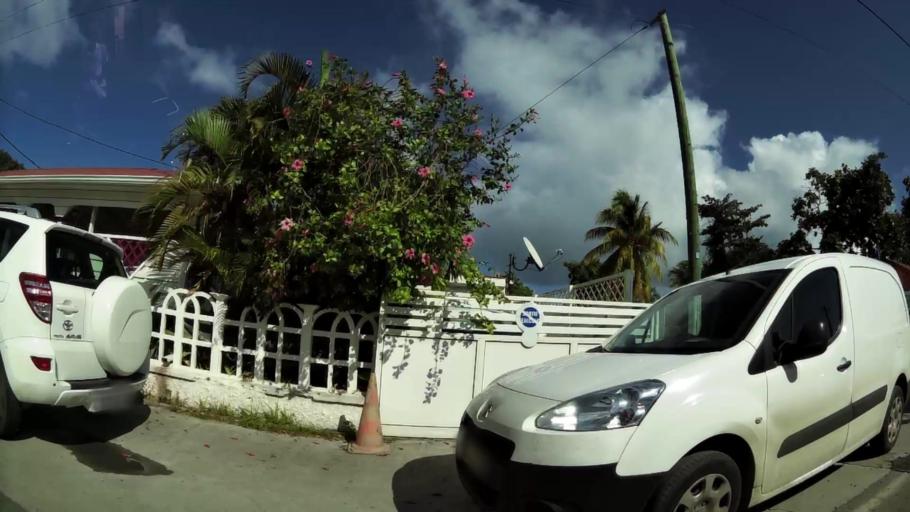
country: GP
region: Guadeloupe
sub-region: Guadeloupe
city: Port-Louis
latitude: 16.4166
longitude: -61.5302
